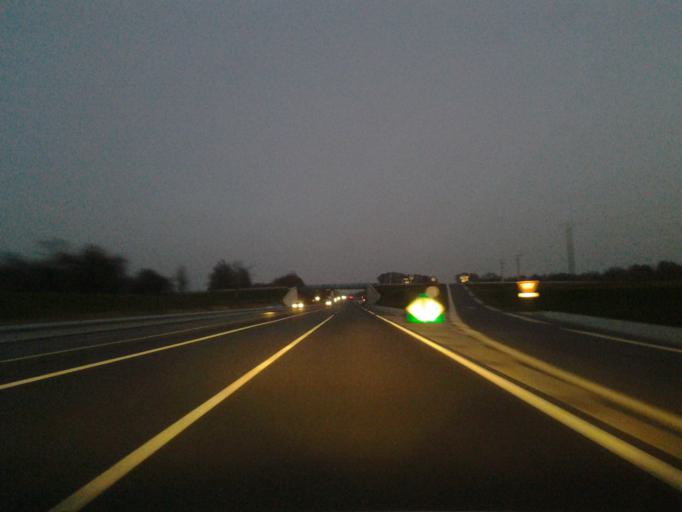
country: FR
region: Pays de la Loire
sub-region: Departement de la Vendee
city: Saint-Christophe-du-Ligneron
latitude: 46.8322
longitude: -1.8204
